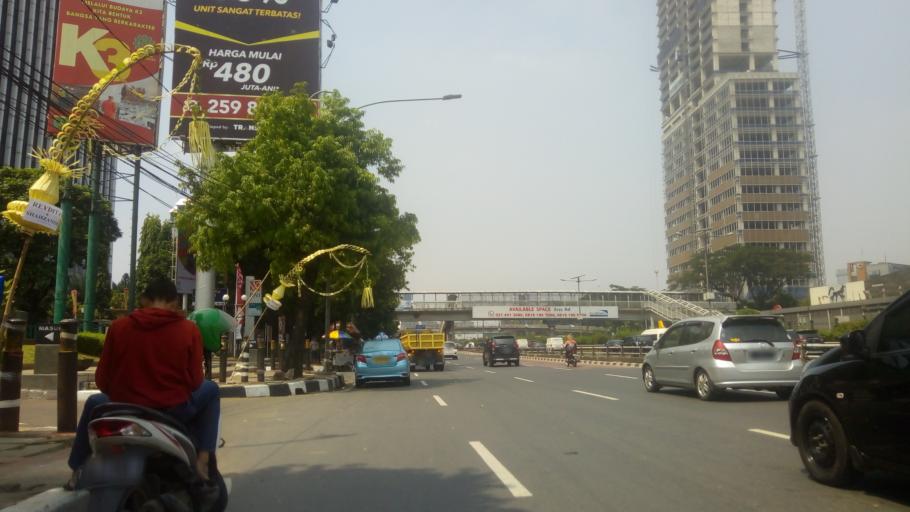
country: ID
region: Jakarta Raya
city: Jakarta
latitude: -6.2380
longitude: 106.8298
